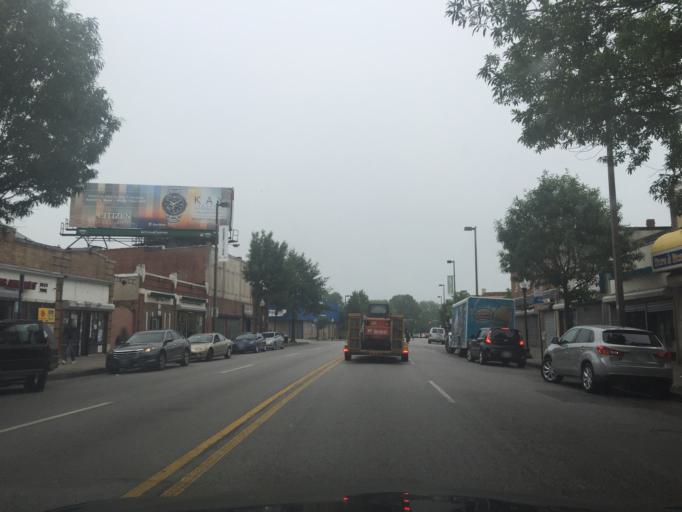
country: US
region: Maryland
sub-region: Baltimore County
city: Lochearn
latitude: 39.3487
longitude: -76.6753
